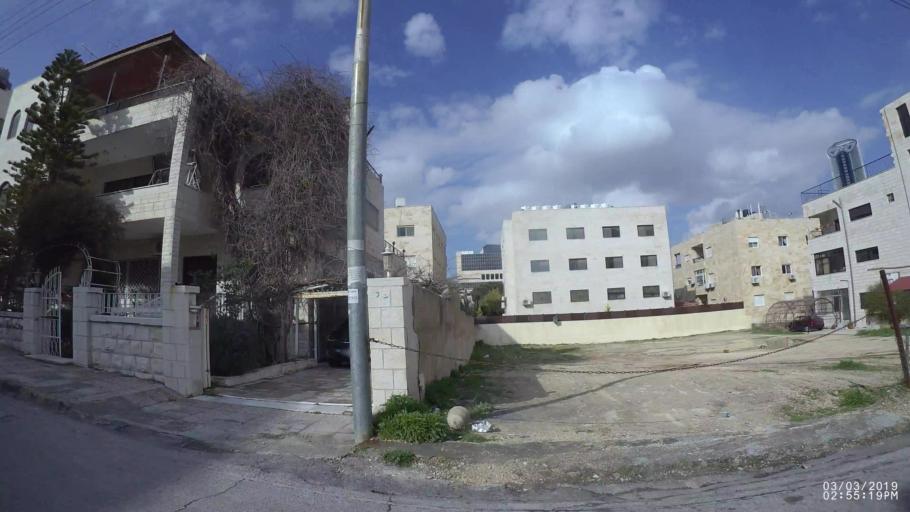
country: JO
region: Amman
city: Amman
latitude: 31.9633
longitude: 35.8973
